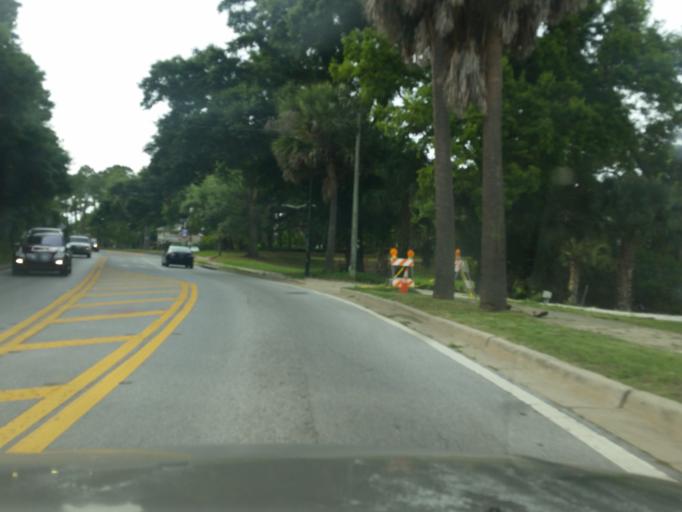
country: US
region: Florida
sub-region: Escambia County
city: East Pensacola Heights
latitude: 30.4207
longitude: -87.1939
